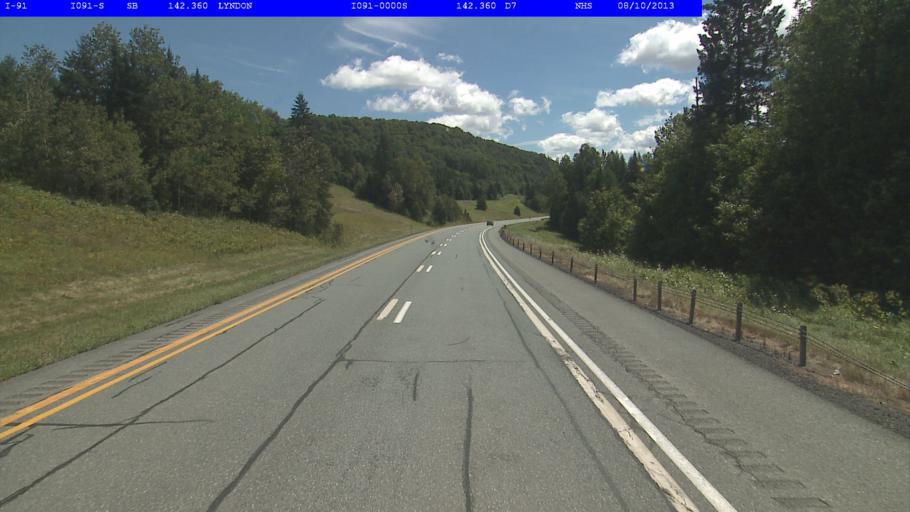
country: US
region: Vermont
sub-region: Caledonia County
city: Lyndonville
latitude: 44.5803
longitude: -72.0554
